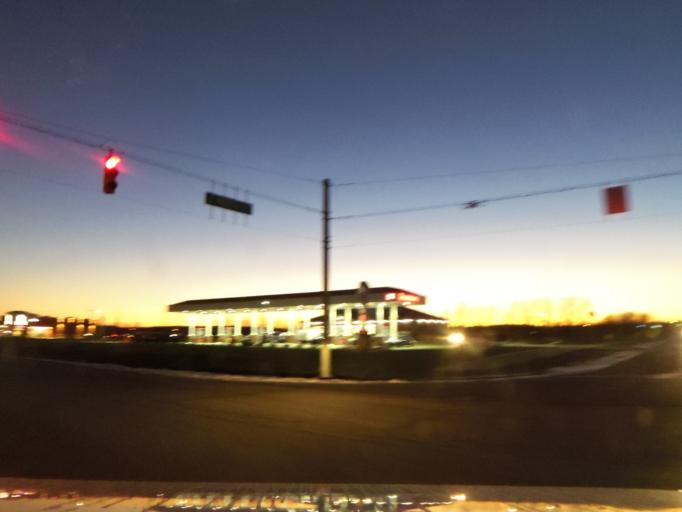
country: US
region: Indiana
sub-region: Lake County
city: Crown Point
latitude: 41.4202
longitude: -87.3354
